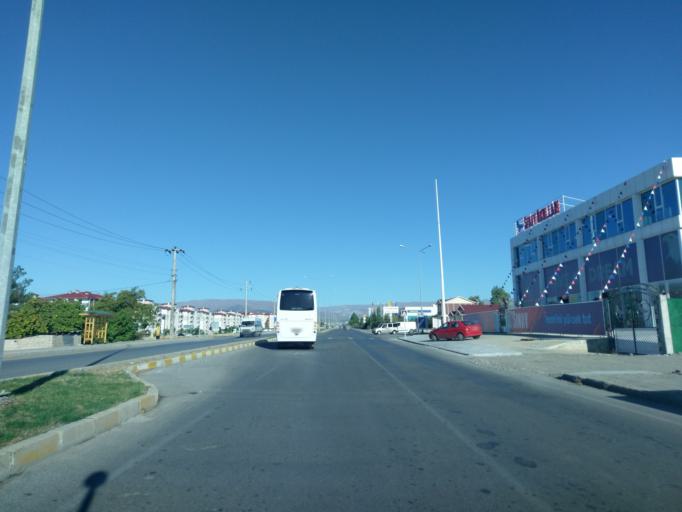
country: TR
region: Erzincan
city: Erzincan
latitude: 39.7559
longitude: 39.4496
